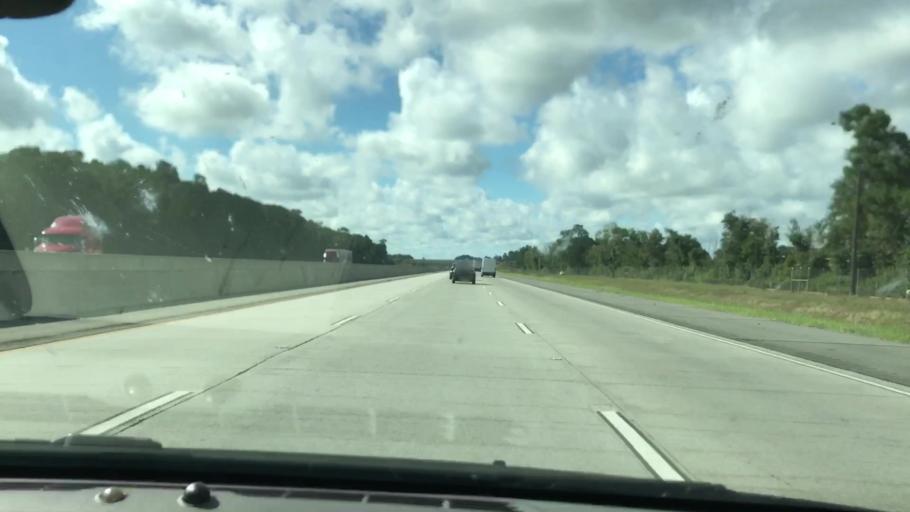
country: US
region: Georgia
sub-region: Tift County
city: Omega
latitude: 31.3002
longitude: -83.4777
